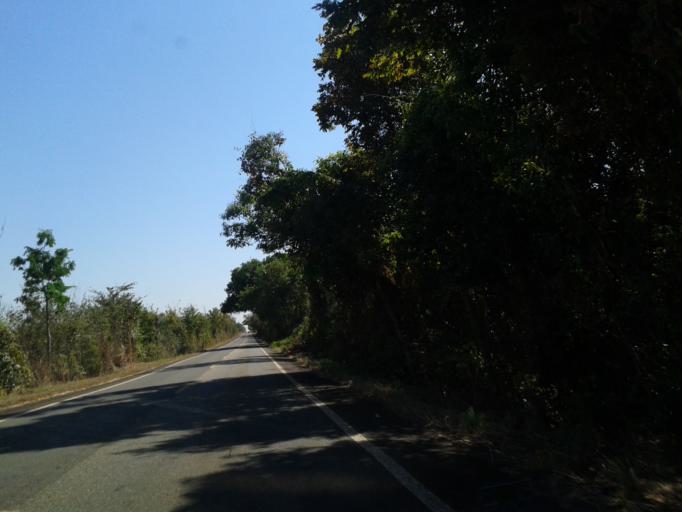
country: BR
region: Goias
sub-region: Sao Miguel Do Araguaia
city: Sao Miguel do Araguaia
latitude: -13.9325
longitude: -50.3205
